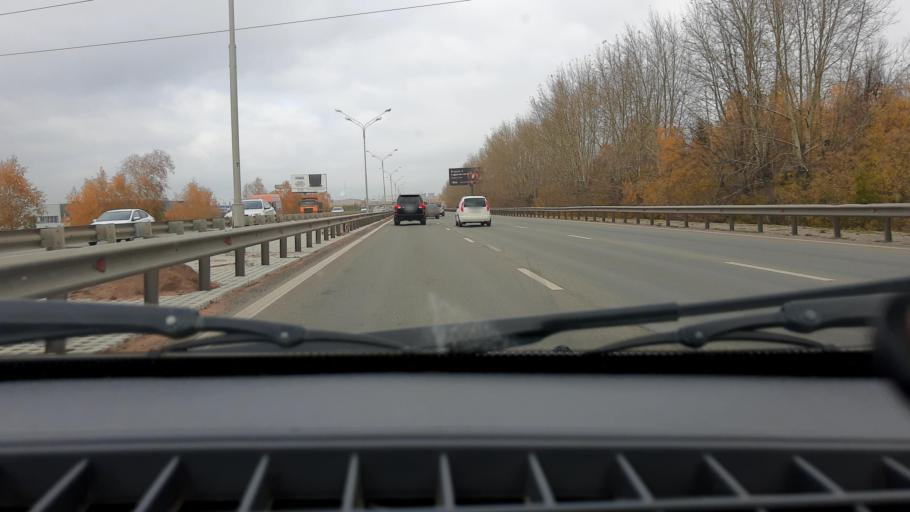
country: RU
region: Bashkortostan
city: Ufa
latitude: 54.6642
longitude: 55.9330
